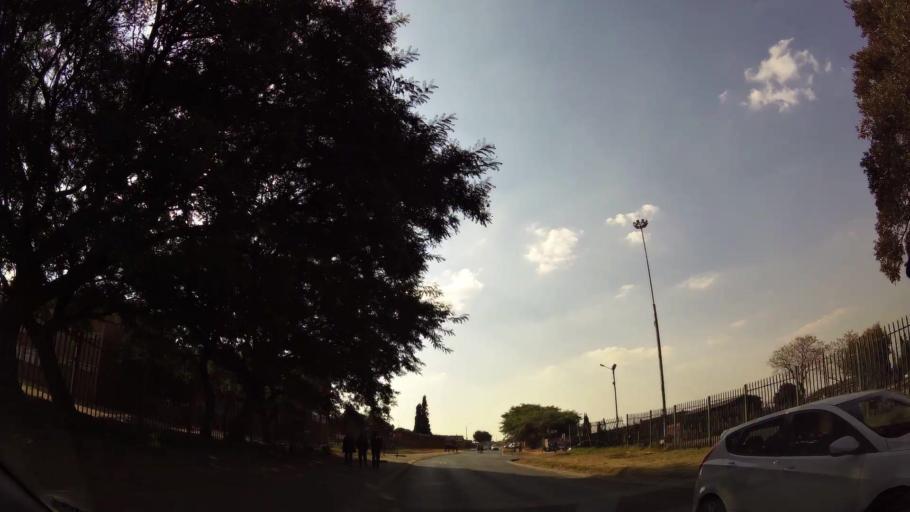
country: ZA
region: Gauteng
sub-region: Ekurhuleni Metropolitan Municipality
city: Benoni
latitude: -26.1557
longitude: 28.4005
